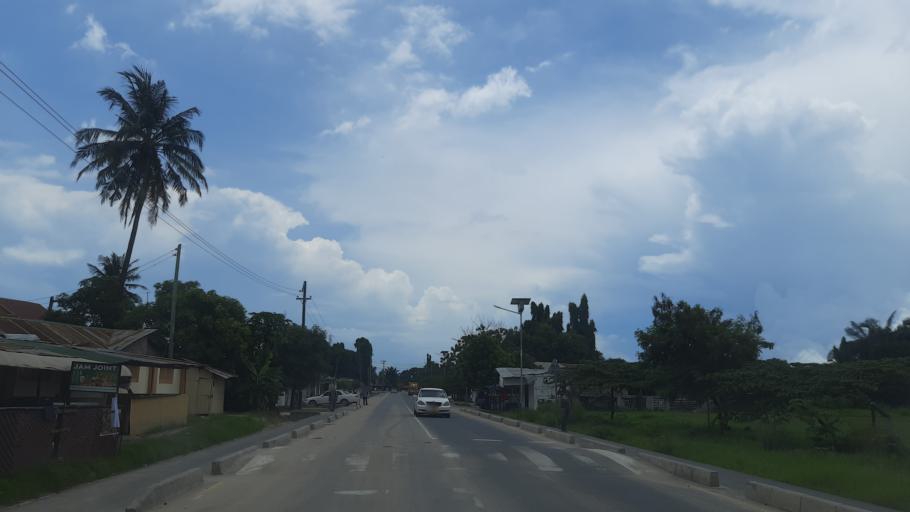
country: TZ
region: Dar es Salaam
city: Magomeni
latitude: -6.7741
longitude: 39.2297
